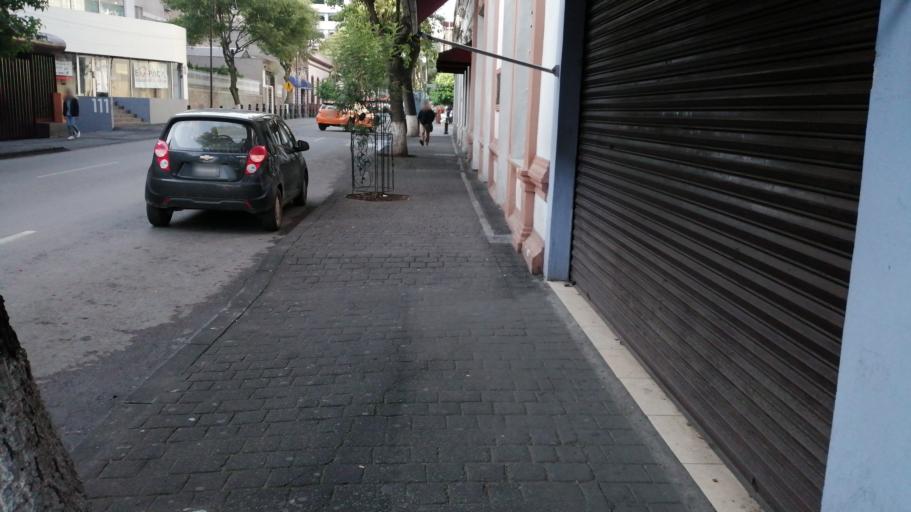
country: MX
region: Mexico
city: Toluca
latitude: 19.2897
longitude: -99.6585
